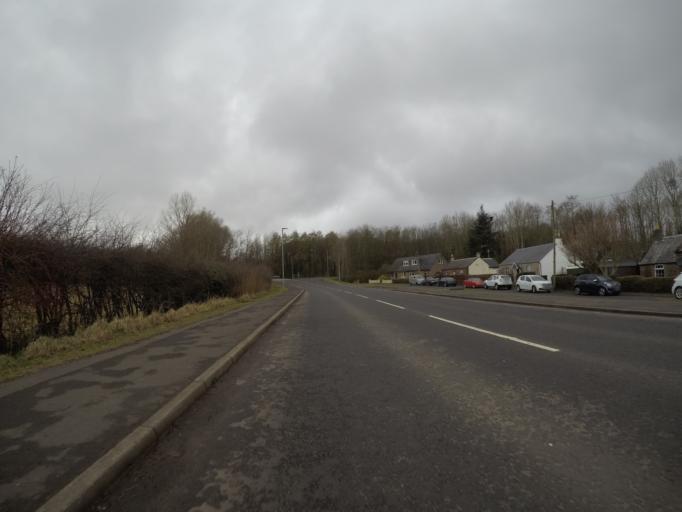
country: GB
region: Scotland
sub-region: North Ayrshire
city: Springside
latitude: 55.6308
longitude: -4.6227
